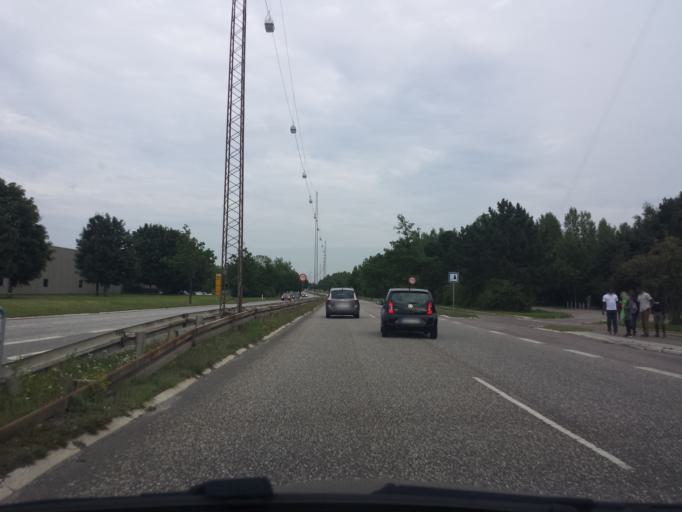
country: DK
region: Capital Region
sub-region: Ballerup Kommune
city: Ballerup
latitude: 55.7220
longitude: 12.3769
